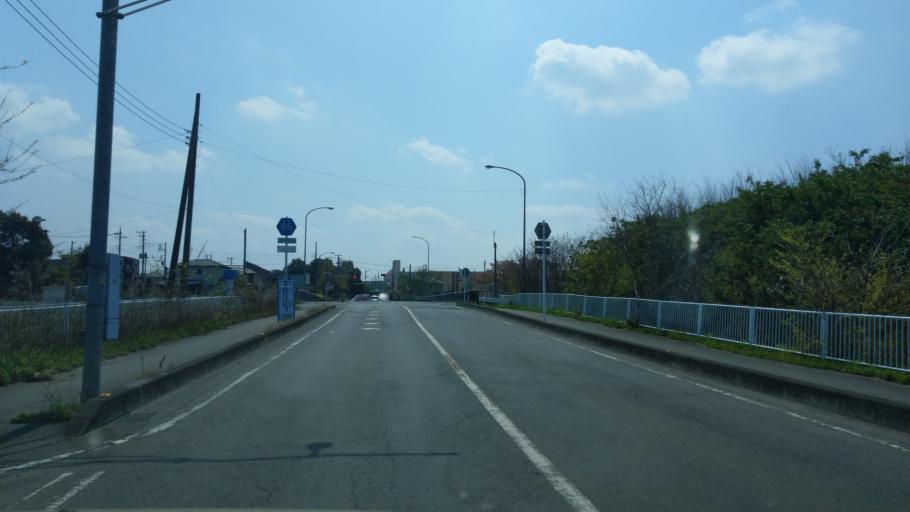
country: JP
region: Saitama
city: Saitama
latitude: 35.8954
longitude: 139.6651
